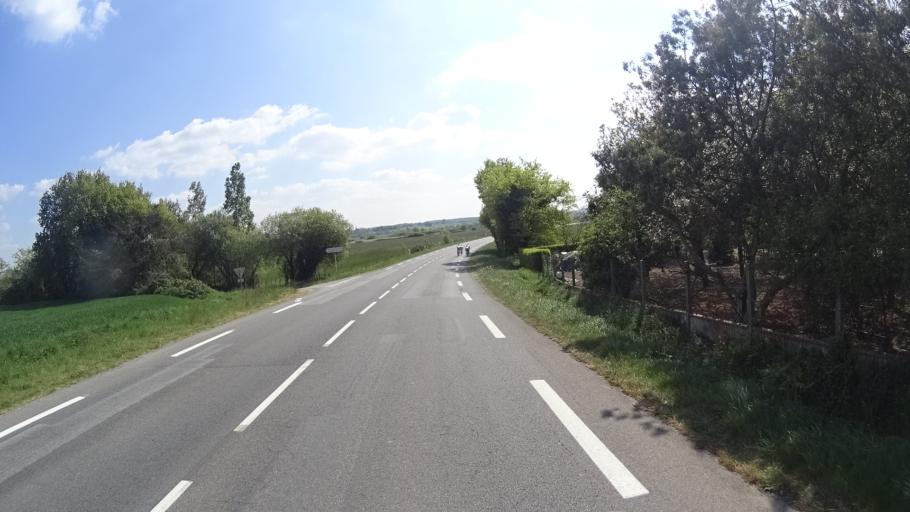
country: FR
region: Brittany
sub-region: Departement du Morbihan
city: Rieux
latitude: 47.5861
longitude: -2.1105
